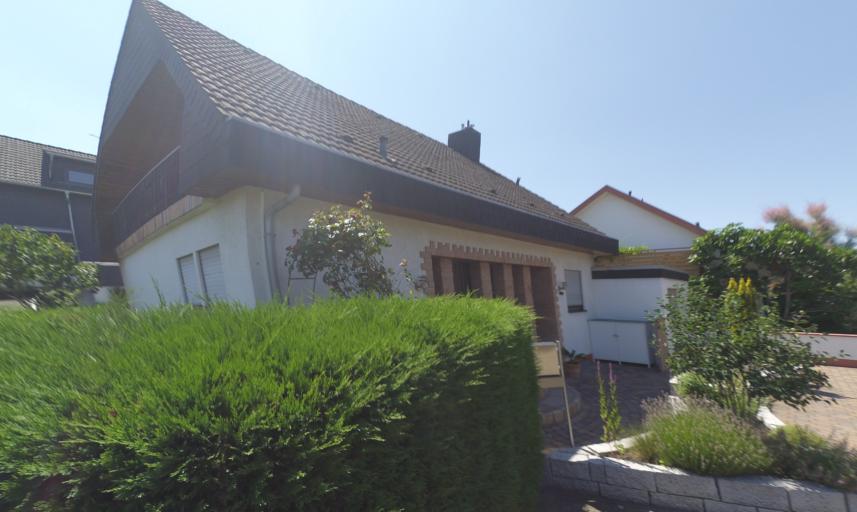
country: DE
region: Rheinland-Pfalz
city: Otterstadt
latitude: 49.3729
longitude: 8.4497
